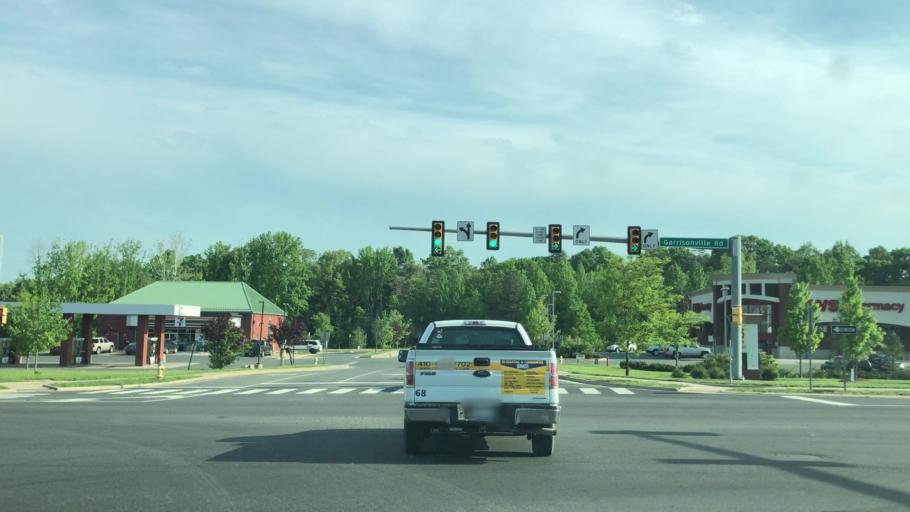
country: US
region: Virginia
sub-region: Stafford County
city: Stafford
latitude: 38.4687
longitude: -77.4608
